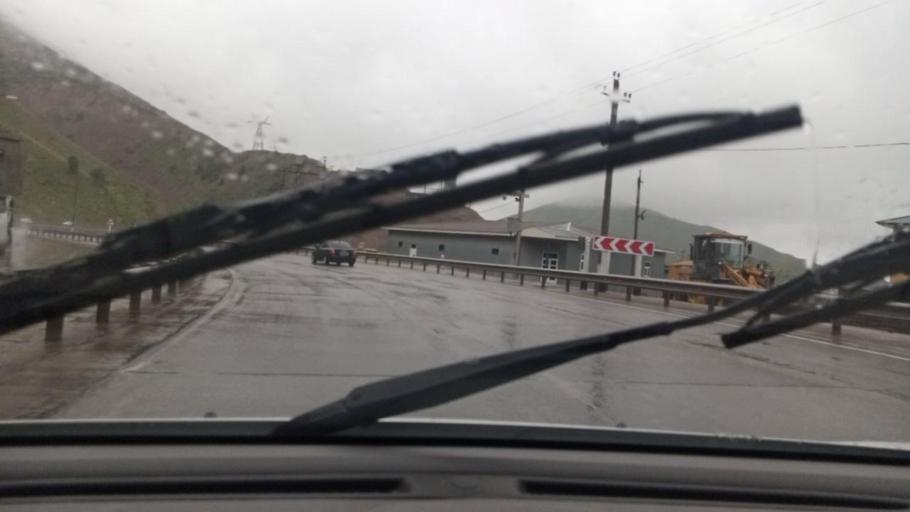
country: UZ
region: Toshkent
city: Angren
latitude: 41.0909
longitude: 70.5320
